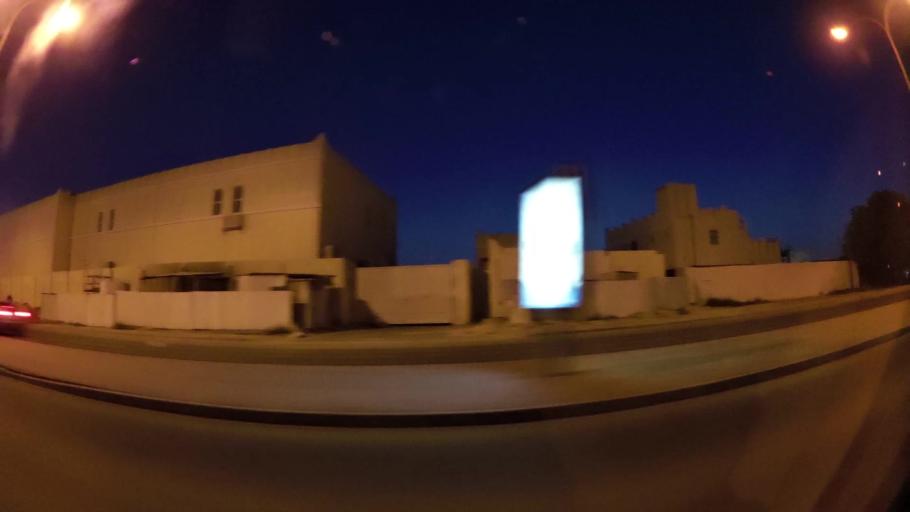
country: QA
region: Baladiyat ar Rayyan
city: Ar Rayyan
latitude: 25.2905
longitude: 51.4309
